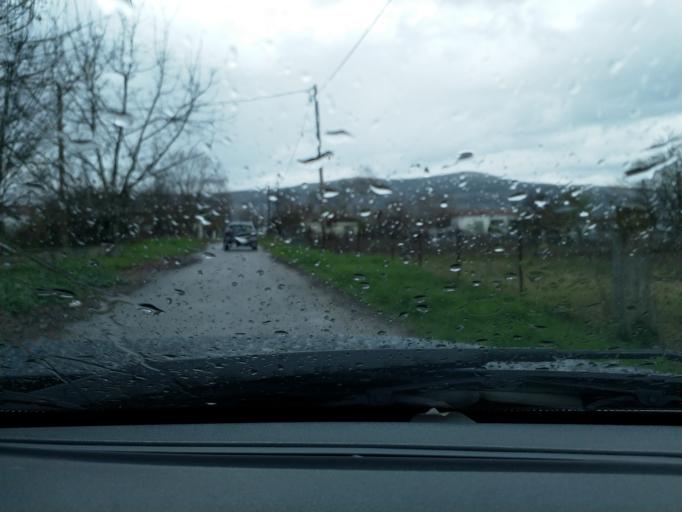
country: GR
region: Thessaly
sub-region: Trikala
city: Taxiarches
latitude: 39.5486
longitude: 21.8957
